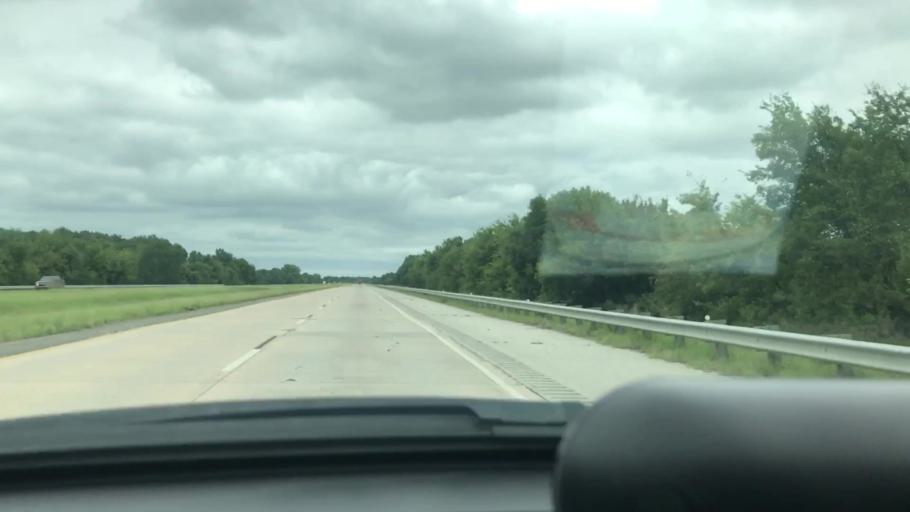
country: US
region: Oklahoma
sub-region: Wagoner County
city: Wagoner
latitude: 35.8926
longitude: -95.4026
